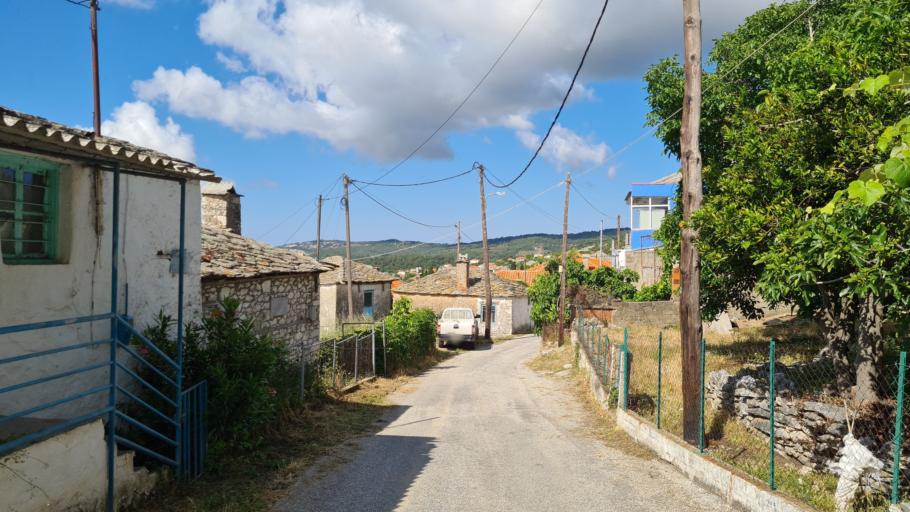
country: GR
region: East Macedonia and Thrace
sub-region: Nomos Kavalas
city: Potamia
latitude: 40.6619
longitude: 24.6993
